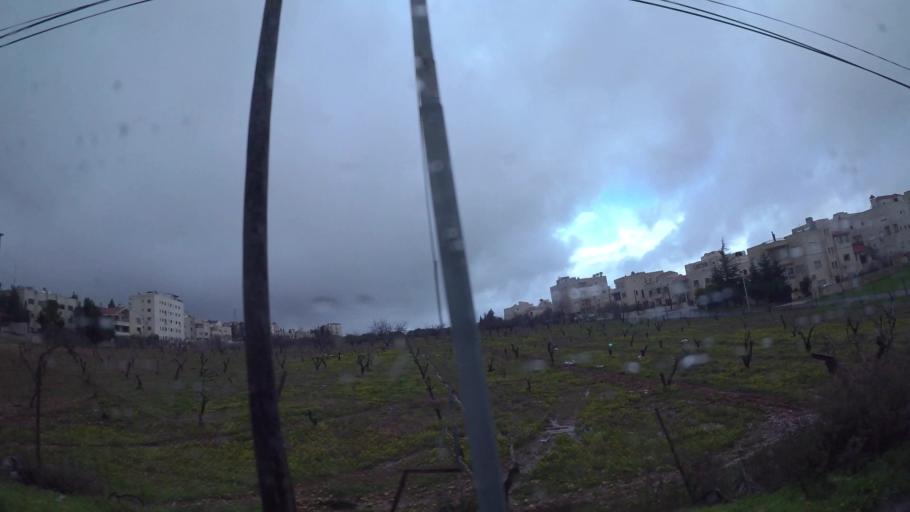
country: JO
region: Amman
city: Al Jubayhah
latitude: 32.0319
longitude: 35.8587
